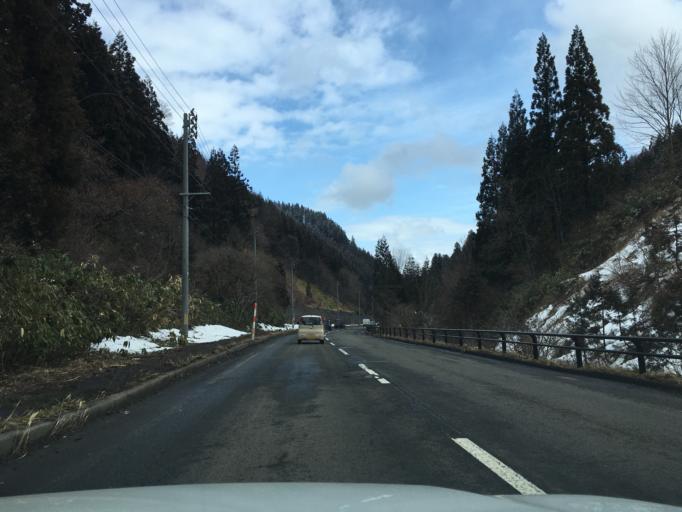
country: JP
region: Akita
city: Takanosu
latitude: 39.9931
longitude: 140.2493
